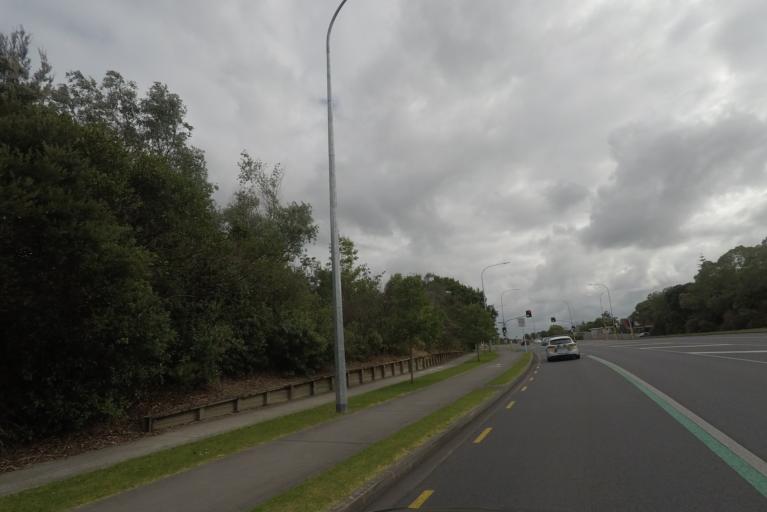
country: NZ
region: Auckland
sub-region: Auckland
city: Rothesay Bay
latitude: -36.7332
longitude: 174.6924
